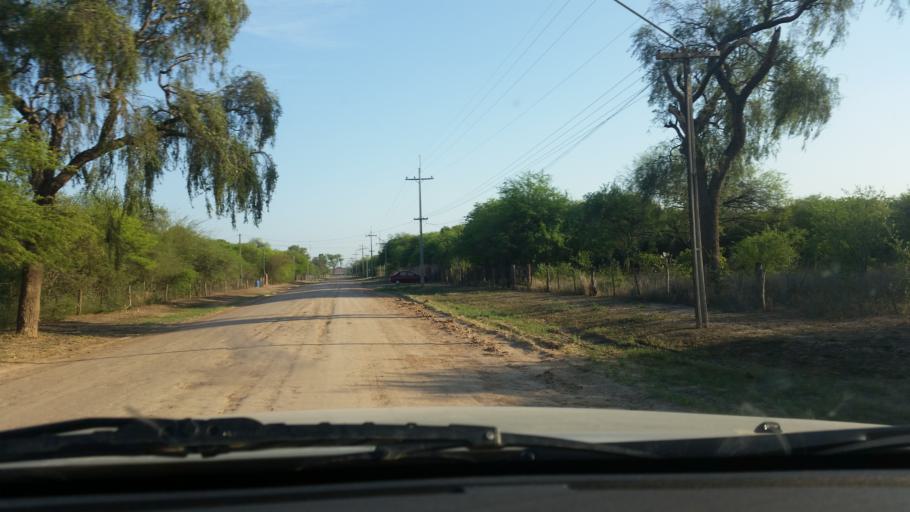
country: PY
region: Boqueron
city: Filadelfia
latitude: -22.3427
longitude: -60.0388
